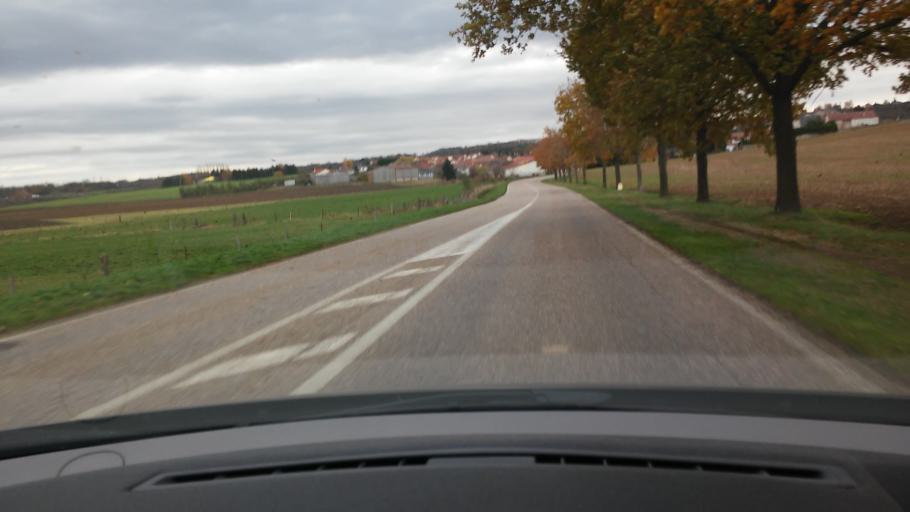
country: FR
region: Lorraine
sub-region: Departement de la Moselle
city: Saint-Julien-les-Metz
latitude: 49.1592
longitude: 6.2332
